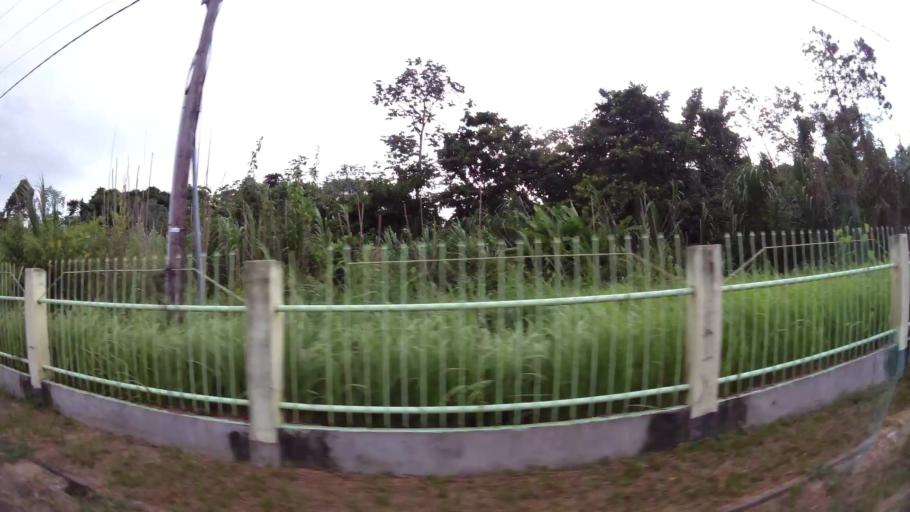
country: SR
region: Paramaribo
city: Paramaribo
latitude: 5.8625
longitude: -55.1769
